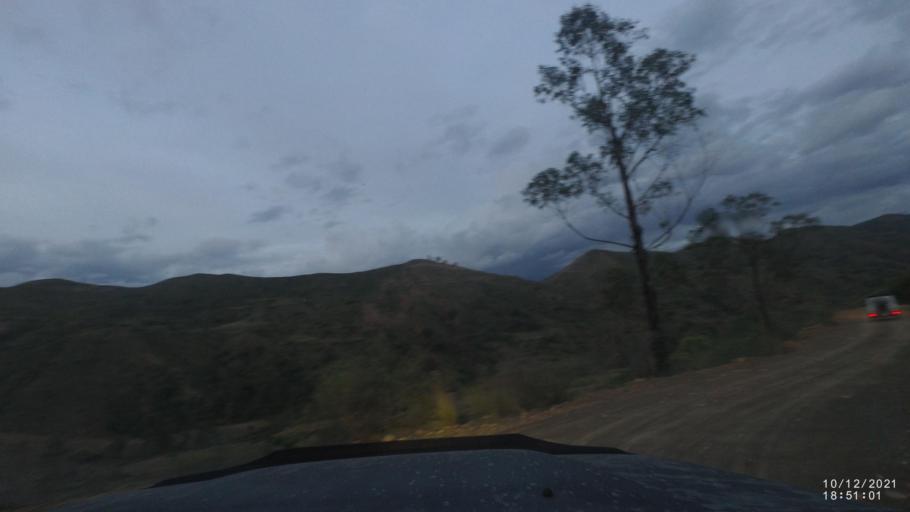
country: BO
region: Cochabamba
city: Tarata
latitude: -17.8811
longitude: -65.9677
